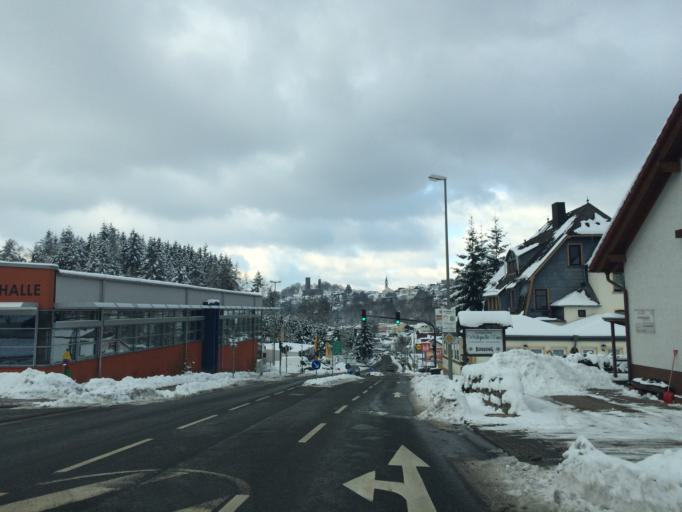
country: DE
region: Hesse
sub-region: Regierungsbezirk Darmstadt
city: Schmitten
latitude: 50.2366
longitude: 8.4337
